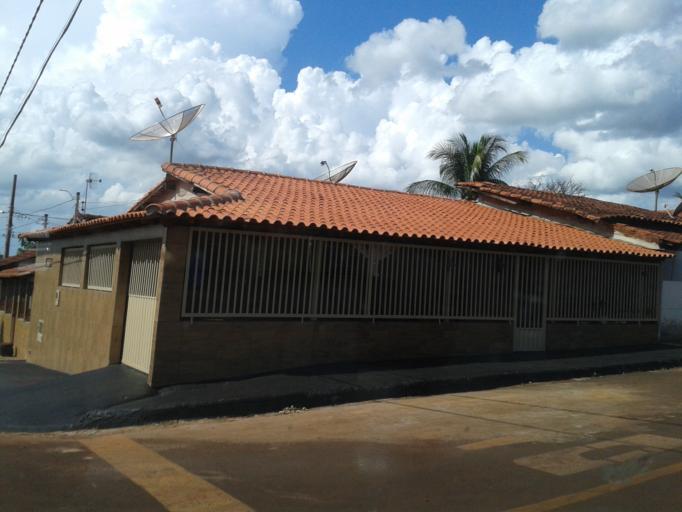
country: BR
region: Minas Gerais
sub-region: Capinopolis
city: Capinopolis
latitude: -18.6854
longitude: -49.5829
